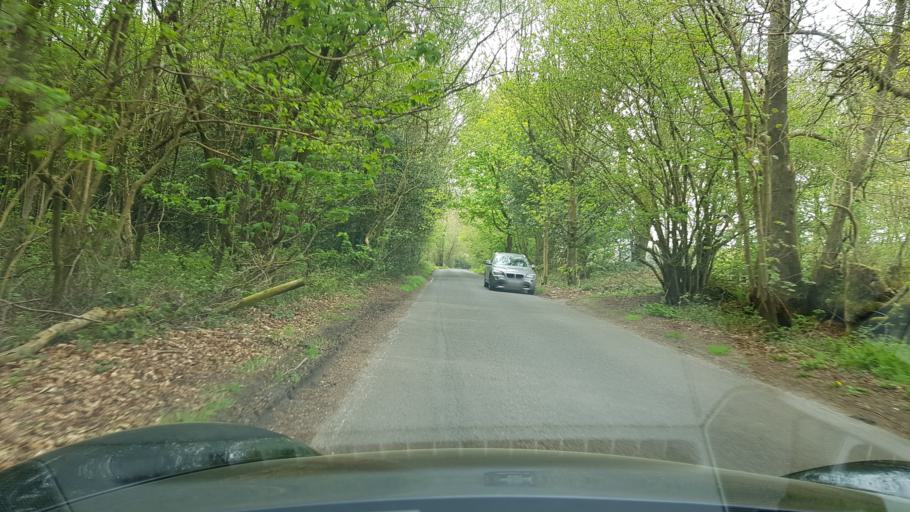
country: GB
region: England
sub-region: Surrey
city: East Horsley
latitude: 51.2342
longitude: -0.4617
